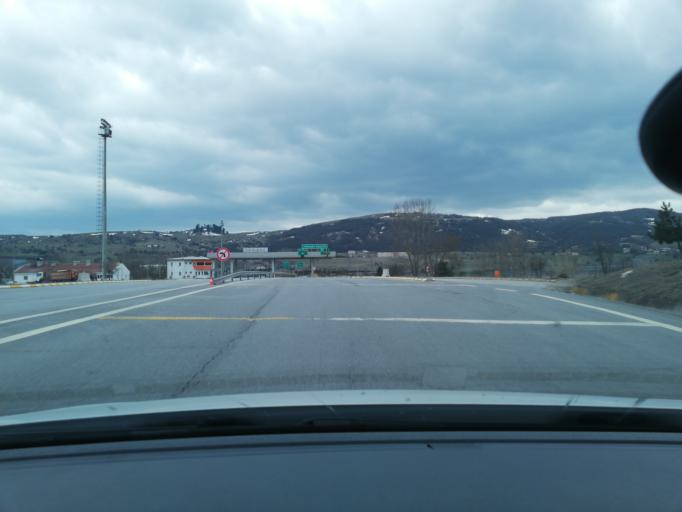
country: TR
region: Bolu
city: Yenicaga
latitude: 40.7696
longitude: 32.0084
